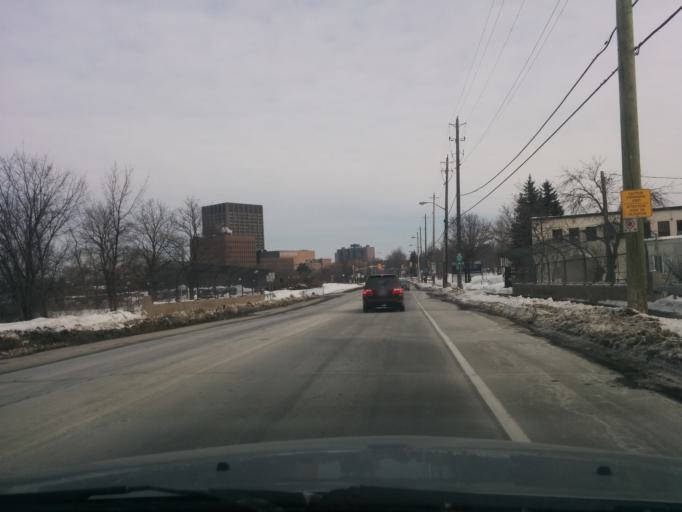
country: CA
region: Ontario
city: Ottawa
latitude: 45.3947
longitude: -75.7081
